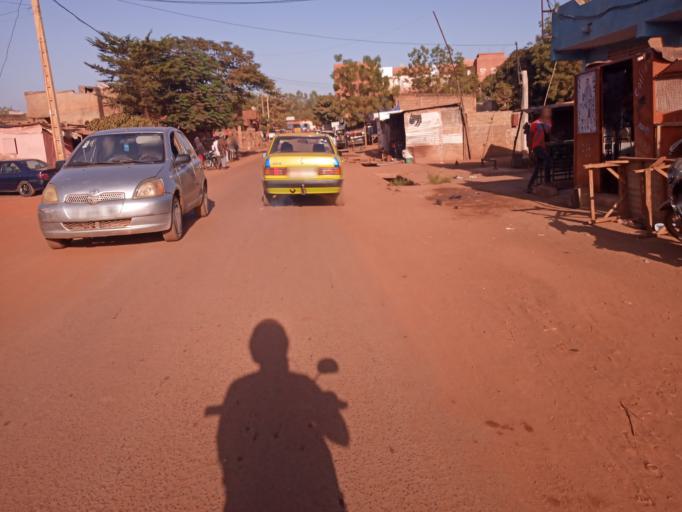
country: ML
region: Bamako
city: Bamako
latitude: 12.6144
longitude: -7.9498
